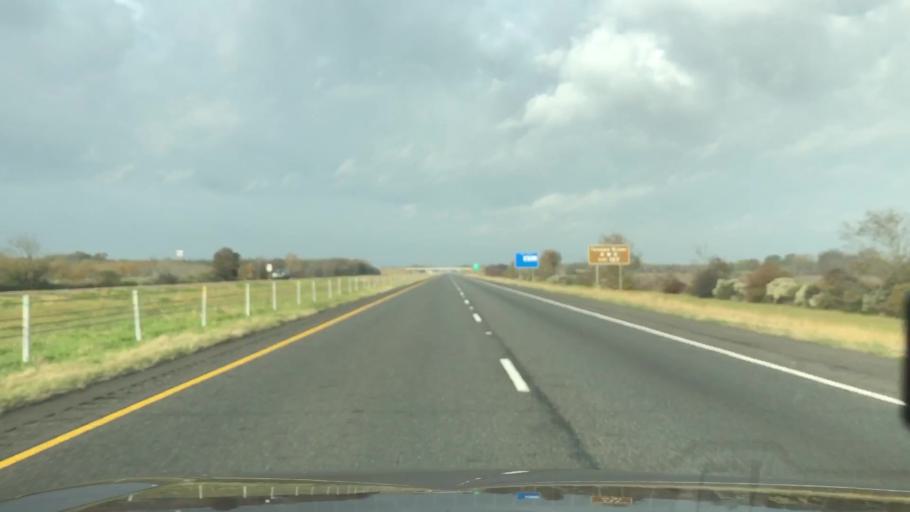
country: US
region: Louisiana
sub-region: Richland Parish
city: Delhi
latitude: 32.4299
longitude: -91.4078
